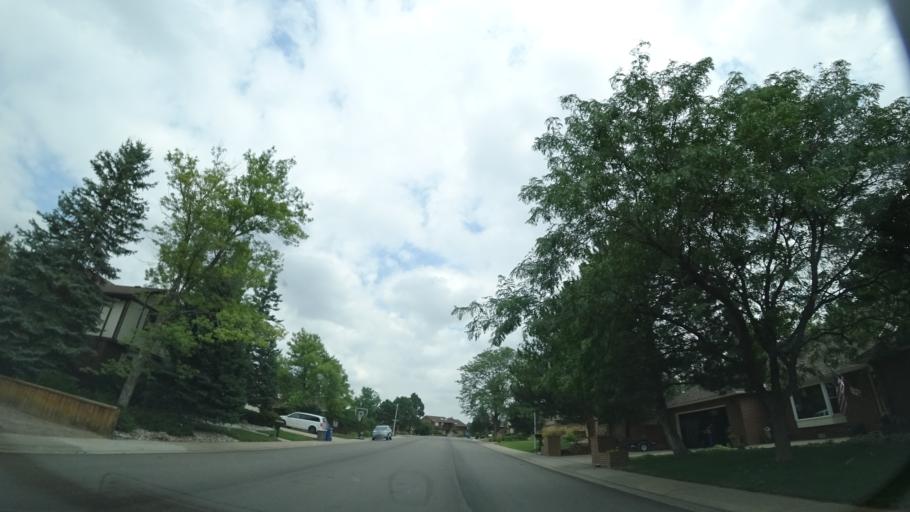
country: US
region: Colorado
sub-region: Jefferson County
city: West Pleasant View
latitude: 39.7151
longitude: -105.1558
